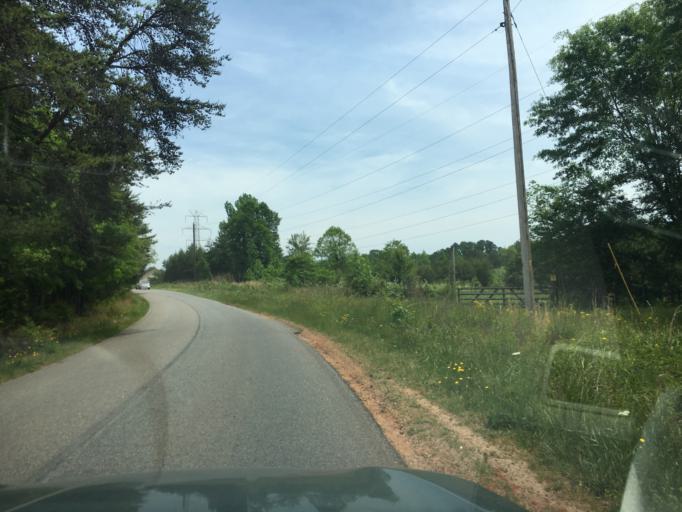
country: US
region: South Carolina
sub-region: Spartanburg County
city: Wellford
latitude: 34.9834
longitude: -82.0855
